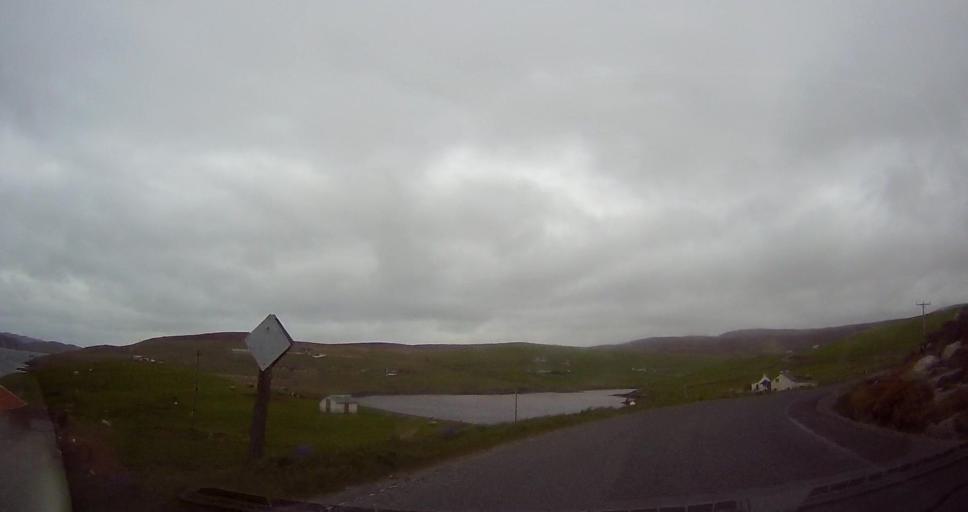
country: GB
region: Scotland
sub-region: Shetland Islands
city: Lerwick
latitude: 60.2988
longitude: -1.3599
